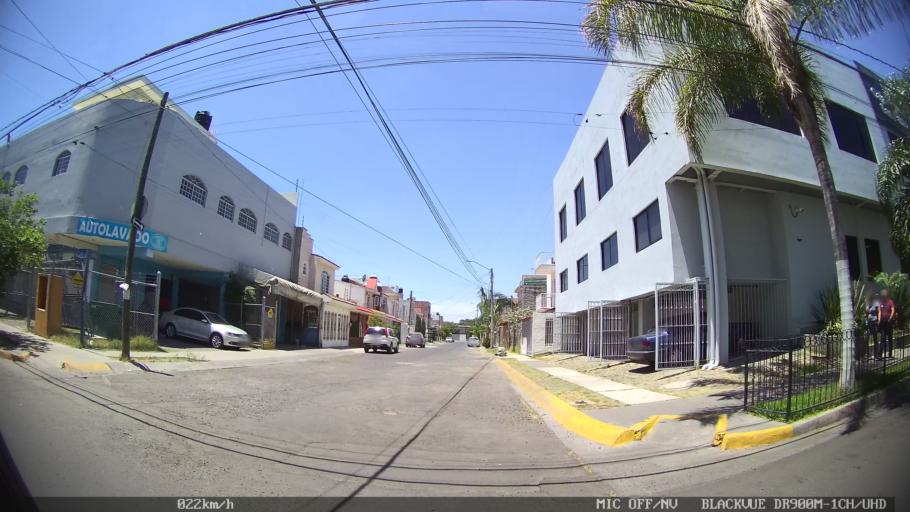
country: MX
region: Jalisco
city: Tlaquepaque
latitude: 20.6788
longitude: -103.2761
